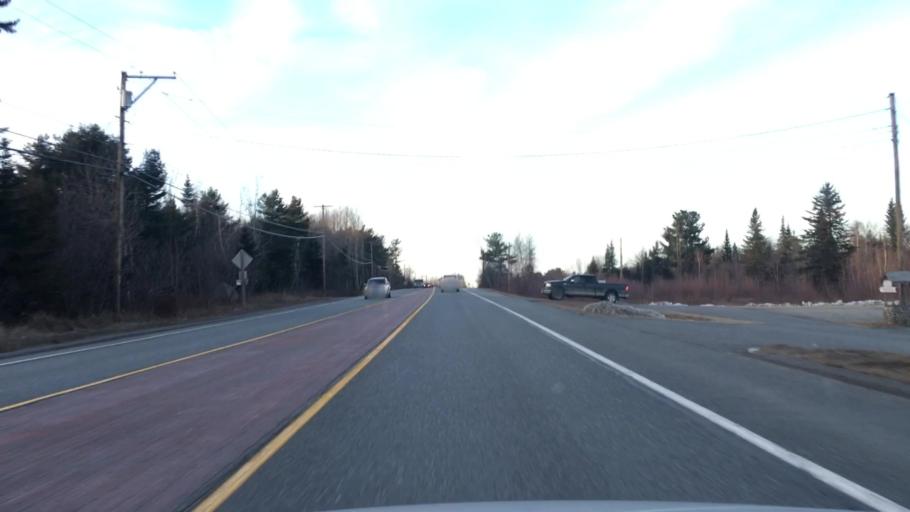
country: US
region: Maine
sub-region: Hancock County
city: Surry
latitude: 44.6174
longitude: -68.5268
